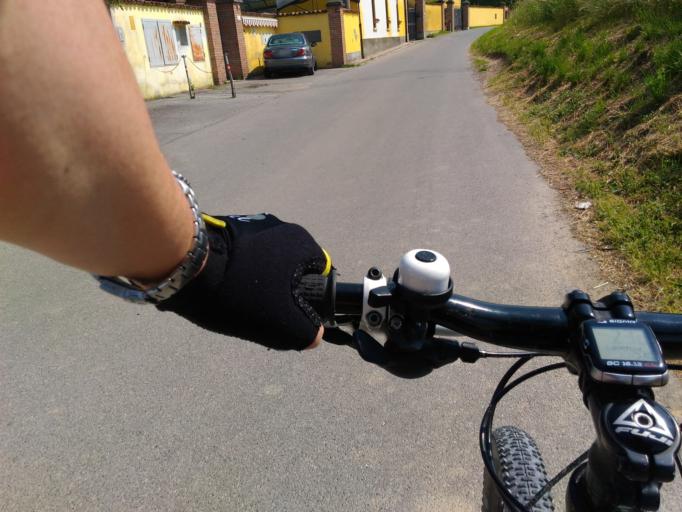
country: IT
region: Lombardy
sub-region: Provincia di Lodi
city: Castiraga Vidardo
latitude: 45.2584
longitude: 9.4148
